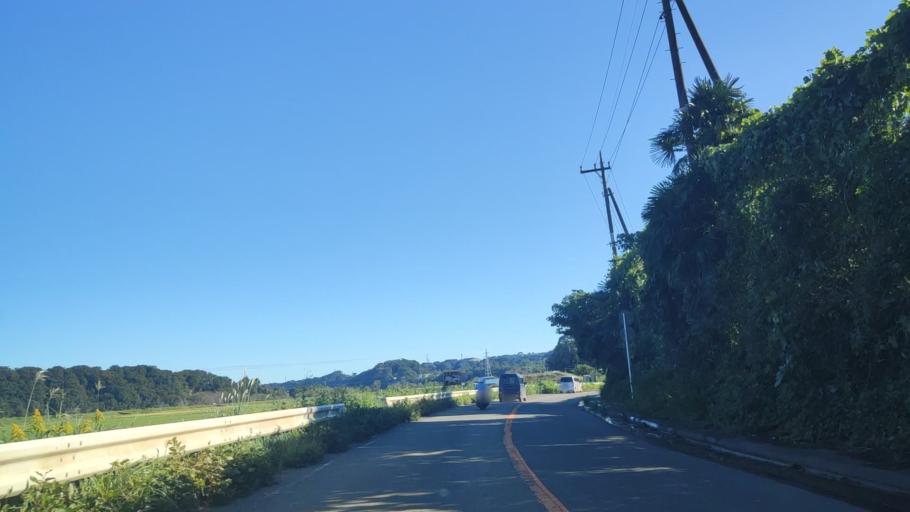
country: JP
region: Kanagawa
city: Zama
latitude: 35.5573
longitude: 139.3194
